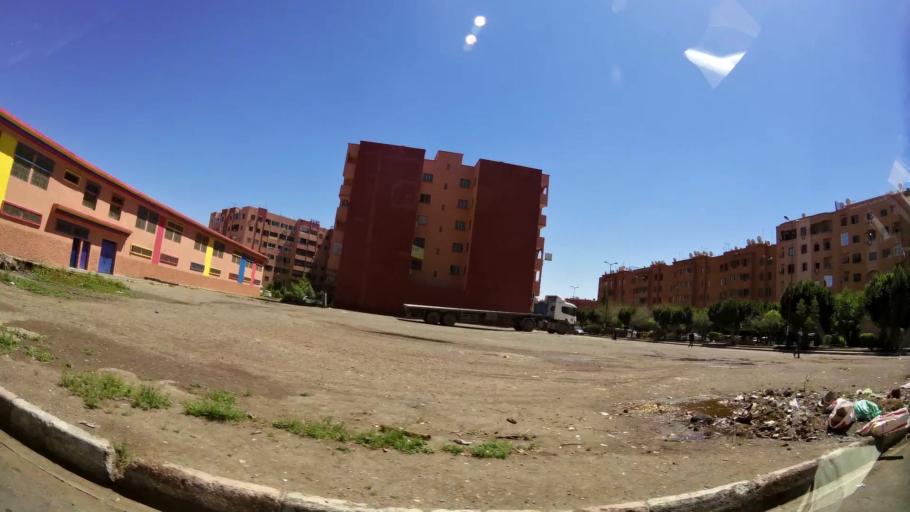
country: MA
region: Marrakech-Tensift-Al Haouz
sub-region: Marrakech
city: Marrakesh
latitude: 31.6345
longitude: -8.0607
